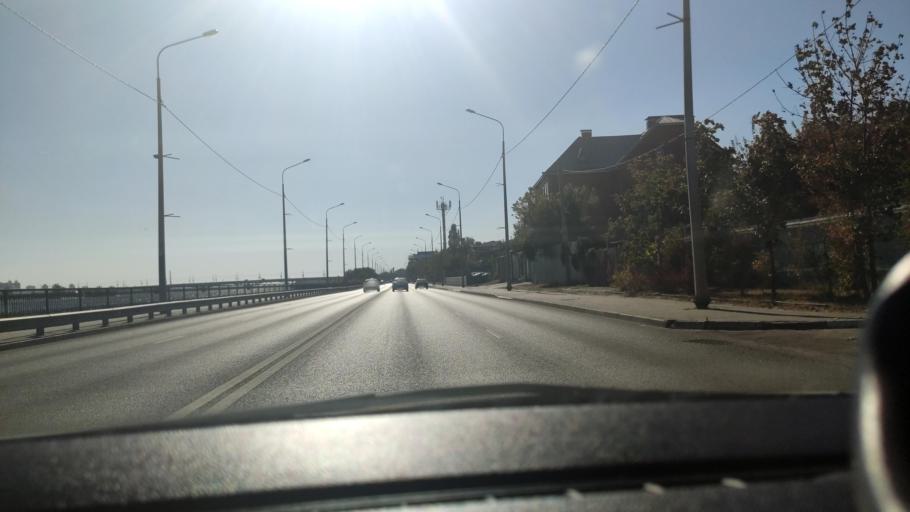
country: RU
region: Voronezj
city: Voronezh
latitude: 51.6762
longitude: 39.2262
